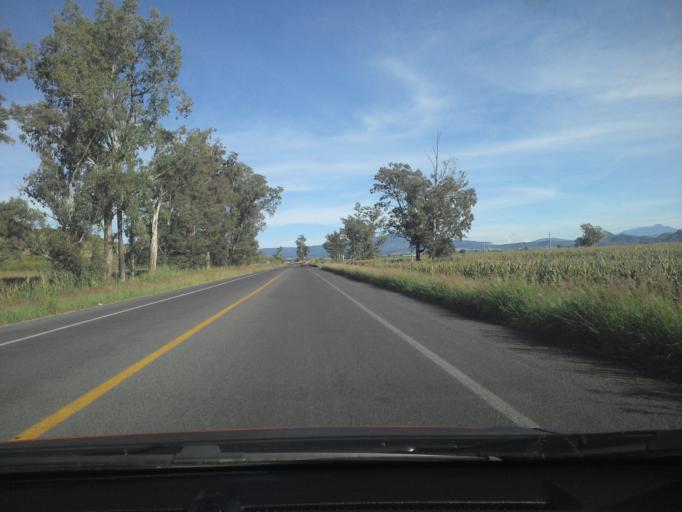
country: MX
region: Jalisco
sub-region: Teuchitlan
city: La Estanzuela
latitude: 20.6662
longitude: -103.7841
